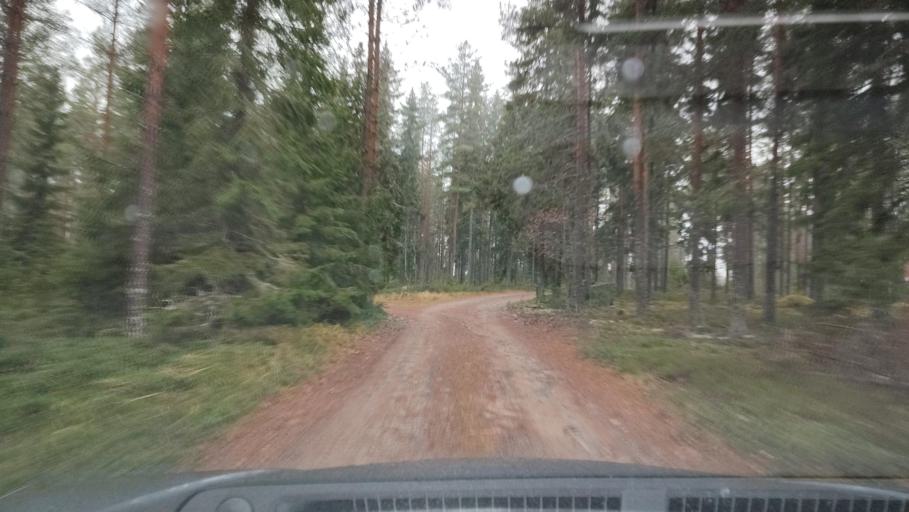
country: FI
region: Southern Ostrobothnia
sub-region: Suupohja
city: Karijoki
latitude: 62.1967
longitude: 21.7844
